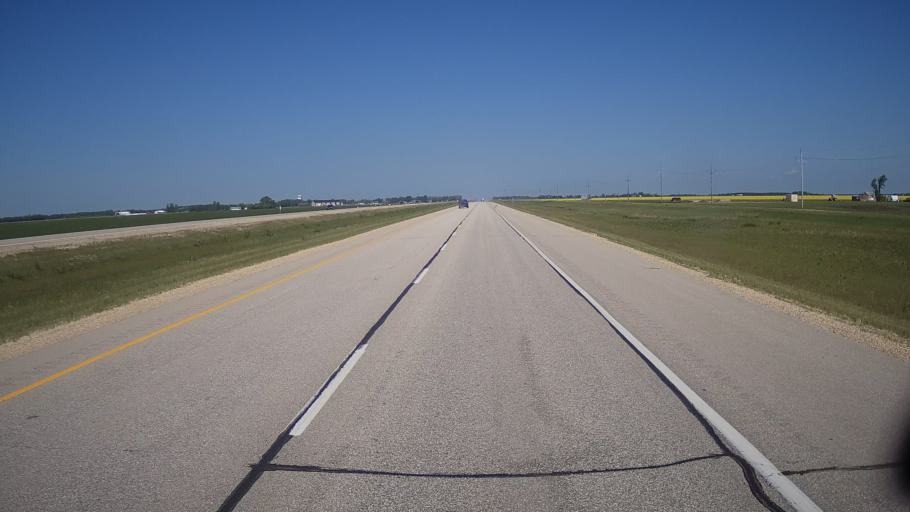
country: CA
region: Manitoba
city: Steinbach
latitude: 49.7196
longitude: -96.6920
